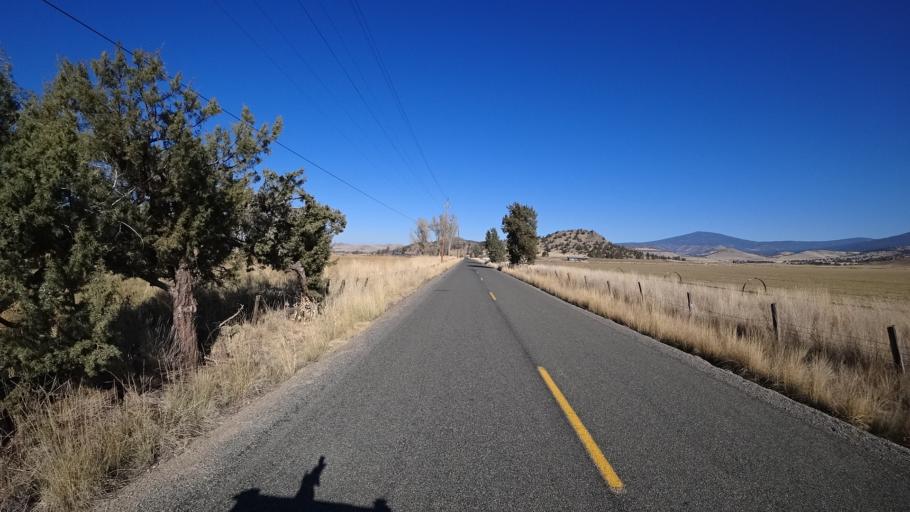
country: US
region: California
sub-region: Siskiyou County
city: Montague
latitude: 41.6819
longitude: -122.3698
